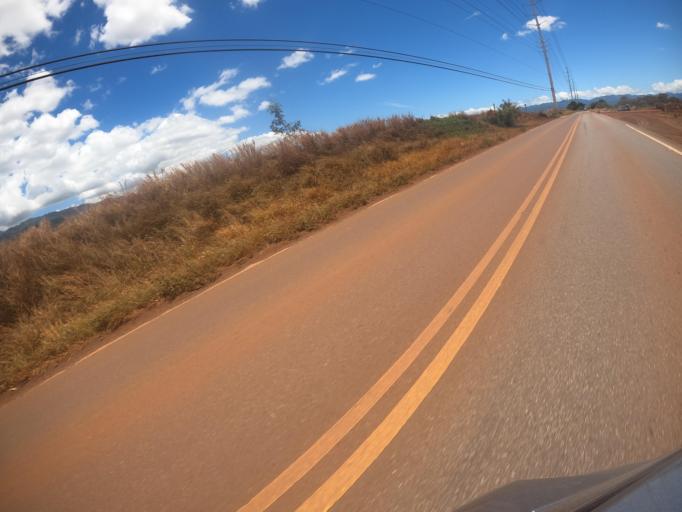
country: US
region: Hawaii
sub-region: Honolulu County
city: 'Ewa Villages
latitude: 21.3679
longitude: -158.0507
